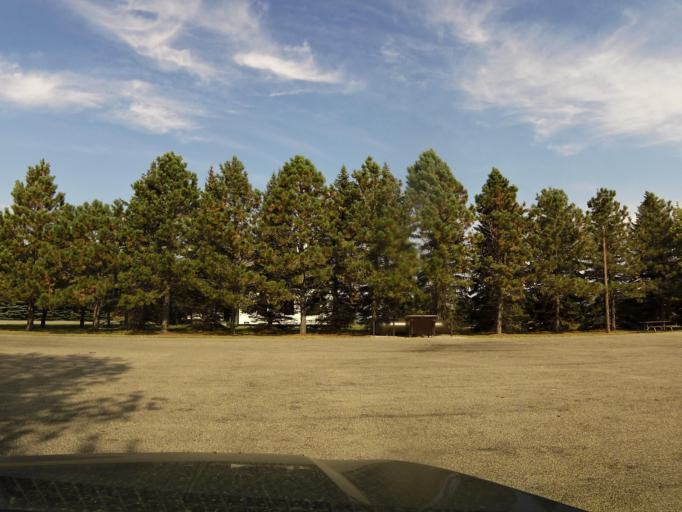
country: US
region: North Dakota
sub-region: Pembina County
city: Cavalier
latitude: 48.7737
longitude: -97.7408
